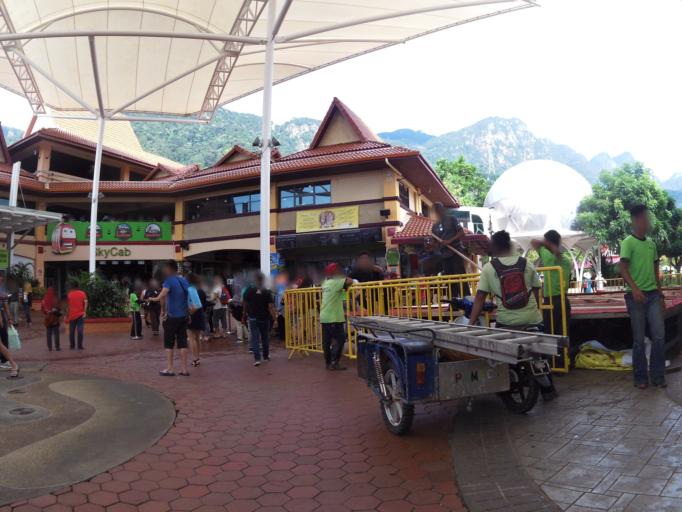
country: MY
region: Kedah
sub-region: Langkawi
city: Kuah
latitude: 6.3711
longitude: 99.6720
